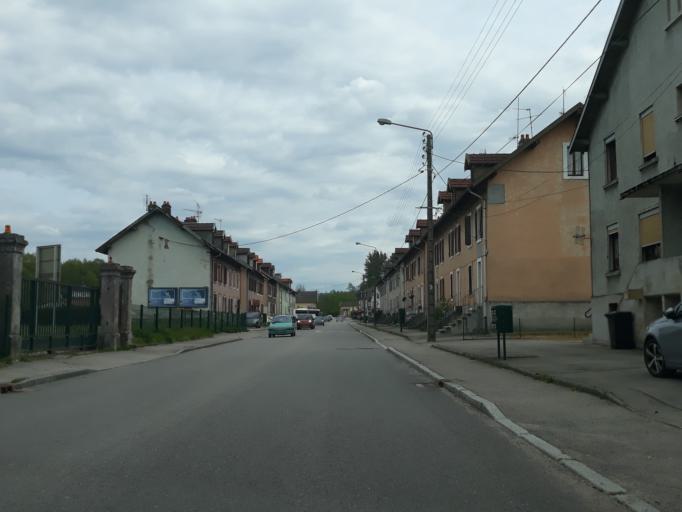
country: FR
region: Lorraine
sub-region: Departement des Vosges
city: Bruyeres
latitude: 48.1814
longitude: 6.7550
